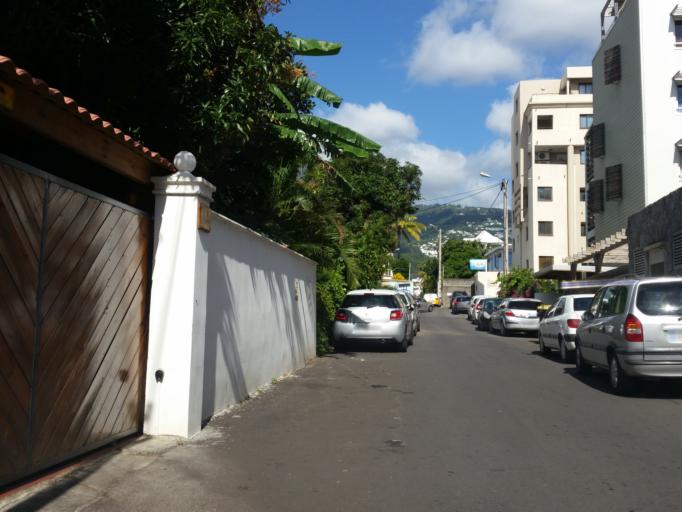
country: RE
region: Reunion
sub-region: Reunion
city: Saint-Denis
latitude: -20.8824
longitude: 55.4609
